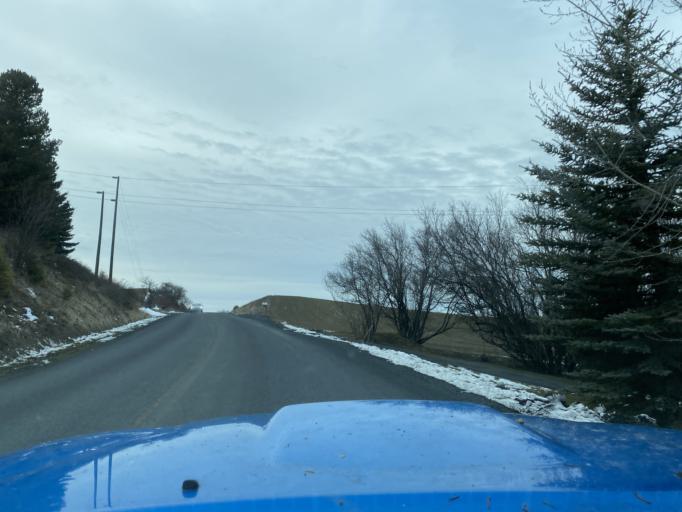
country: US
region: Idaho
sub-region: Latah County
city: Moscow
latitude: 46.7120
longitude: -116.9527
